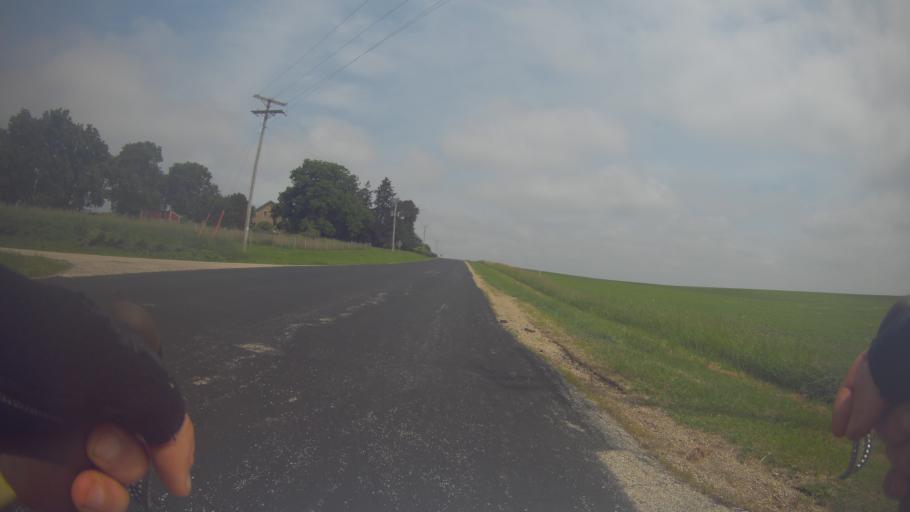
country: US
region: Wisconsin
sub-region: Rock County
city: Edgerton
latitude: 42.9058
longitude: -89.0427
